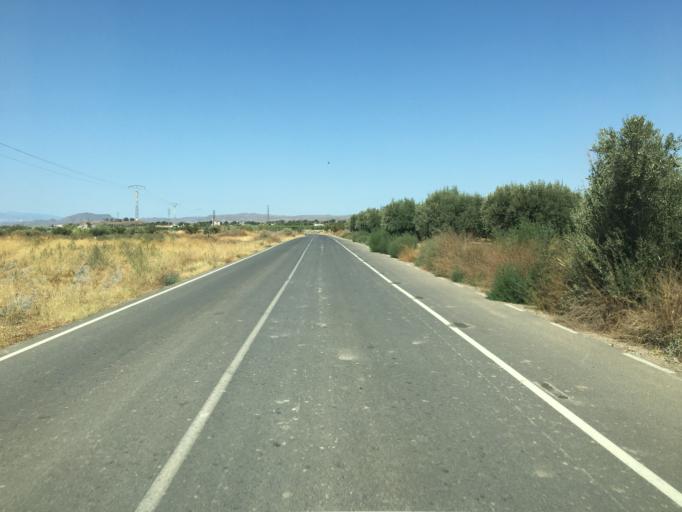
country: ES
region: Andalusia
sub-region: Provincia de Almeria
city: Huercal-Overa
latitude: 37.4214
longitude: -1.8990
